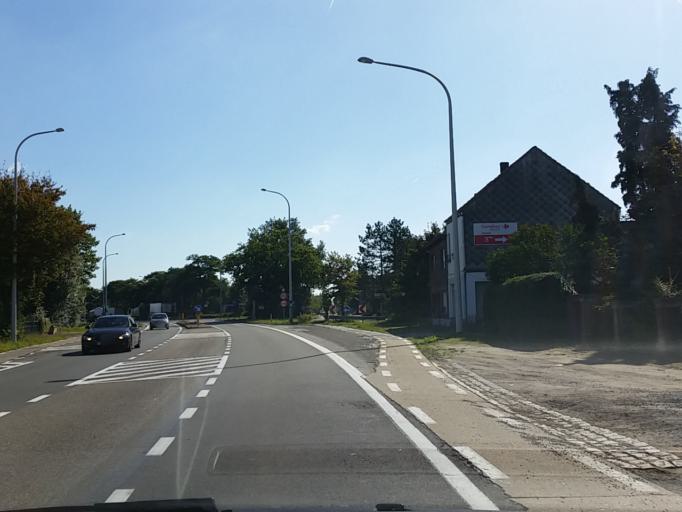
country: BE
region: Flanders
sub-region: Provincie Vlaams-Brabant
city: Herent
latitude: 50.9134
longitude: 4.6590
